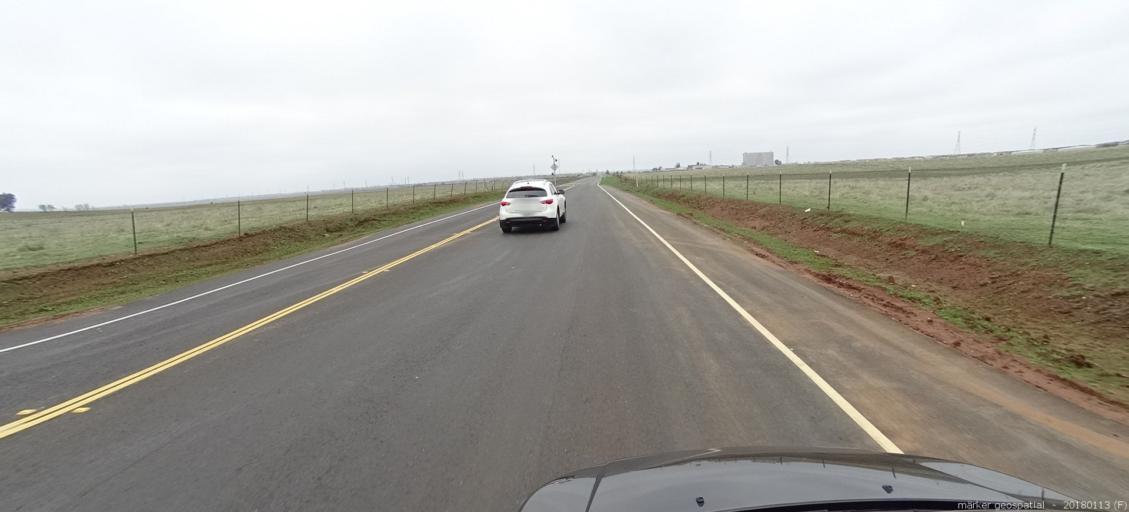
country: US
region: California
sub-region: Sacramento County
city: Gold River
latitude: 38.5592
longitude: -121.1883
